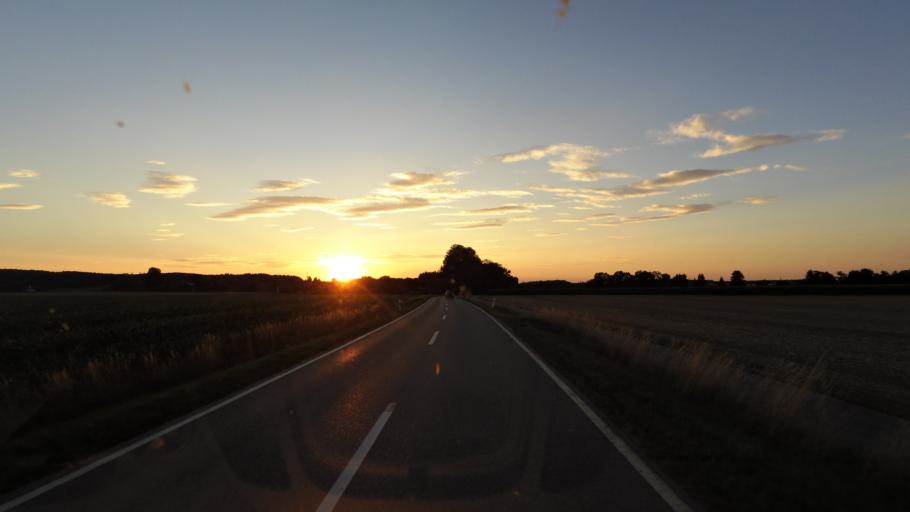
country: DE
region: Bavaria
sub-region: Upper Bavaria
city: Taufkirchen
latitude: 48.1349
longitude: 12.4584
